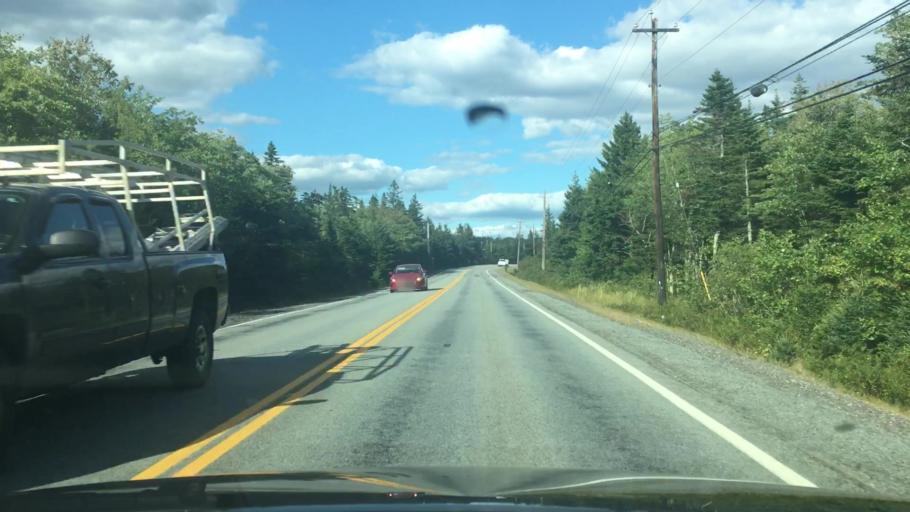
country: CA
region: Nova Scotia
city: Halifax
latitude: 44.5946
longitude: -63.6958
